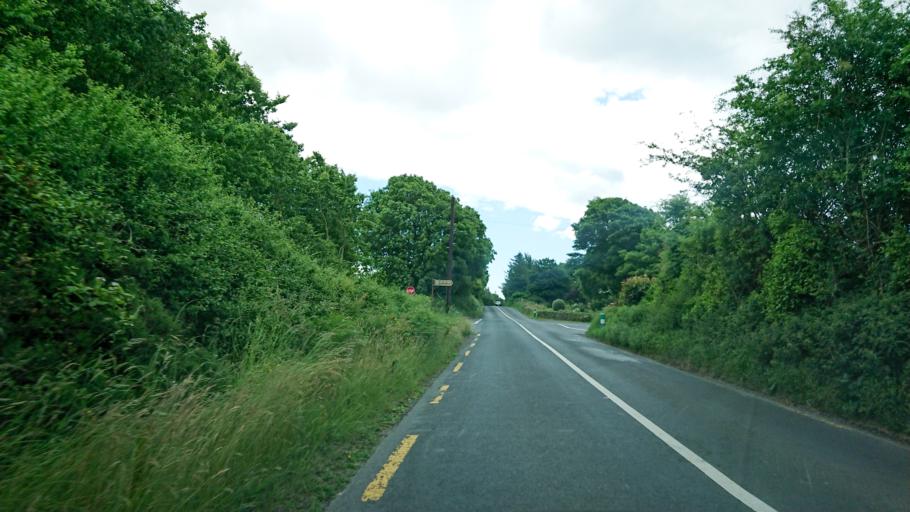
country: IE
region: Munster
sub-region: Waterford
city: Tra Mhor
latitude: 52.1832
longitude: -7.1737
